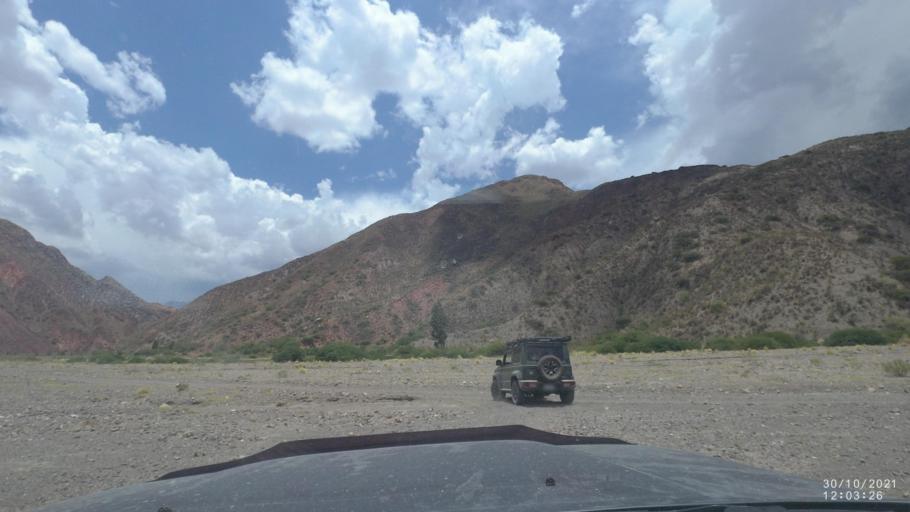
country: BO
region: Cochabamba
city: Colchani
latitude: -17.5268
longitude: -66.6204
